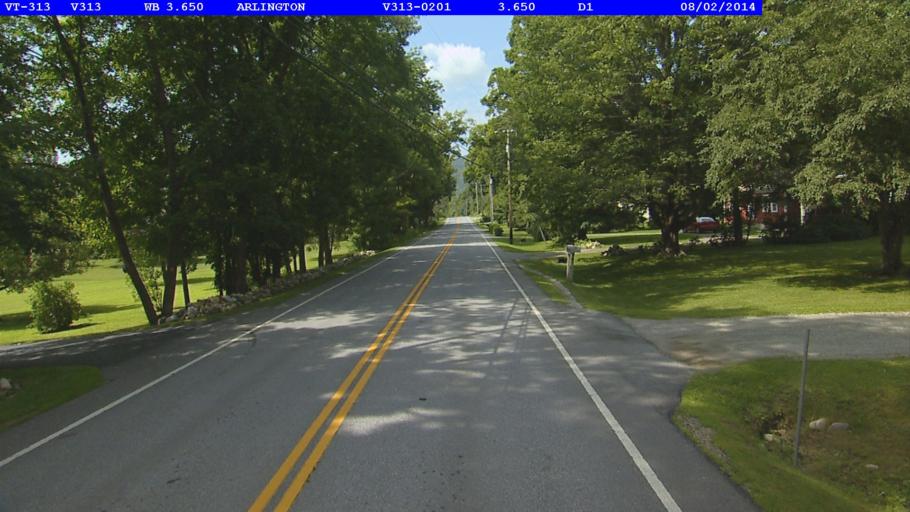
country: US
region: Vermont
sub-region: Bennington County
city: Arlington
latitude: 43.0952
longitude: -73.2014
